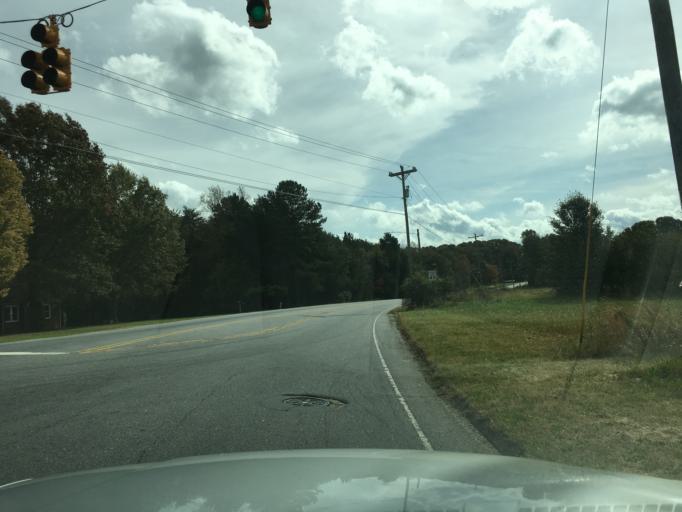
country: US
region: North Carolina
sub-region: Catawba County
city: Newton
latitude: 35.6577
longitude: -81.2665
